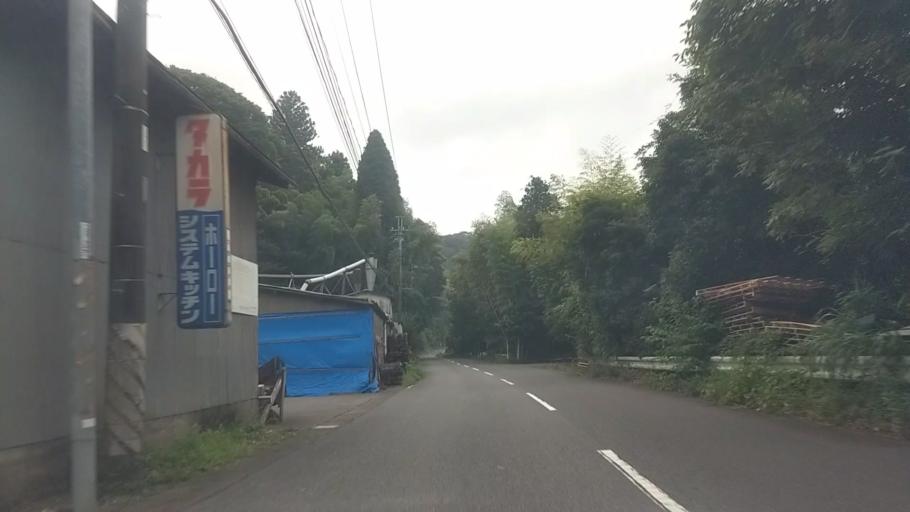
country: JP
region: Chiba
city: Katsuura
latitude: 35.2432
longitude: 140.2427
